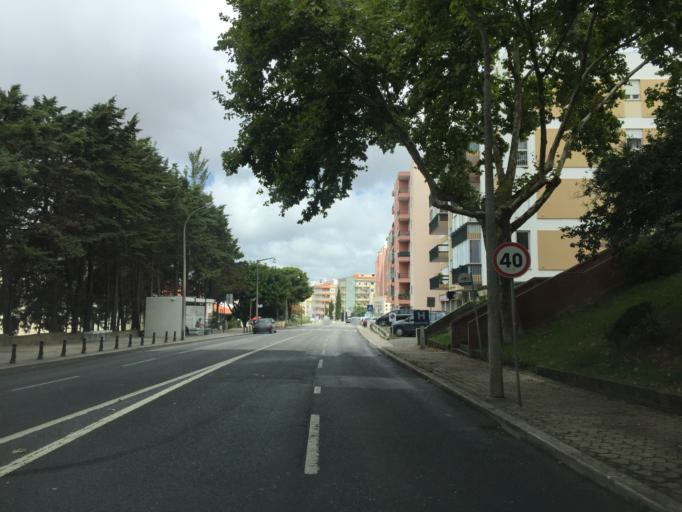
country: PT
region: Lisbon
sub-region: Torres Vedras
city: Torres Vedras
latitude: 39.0851
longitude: -9.2563
